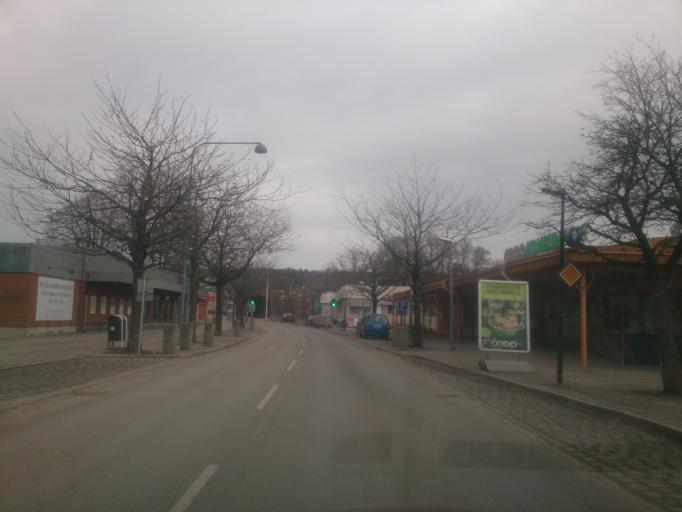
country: SE
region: OEstergoetland
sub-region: Norrkopings Kommun
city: Jursla
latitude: 58.6647
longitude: 16.1814
